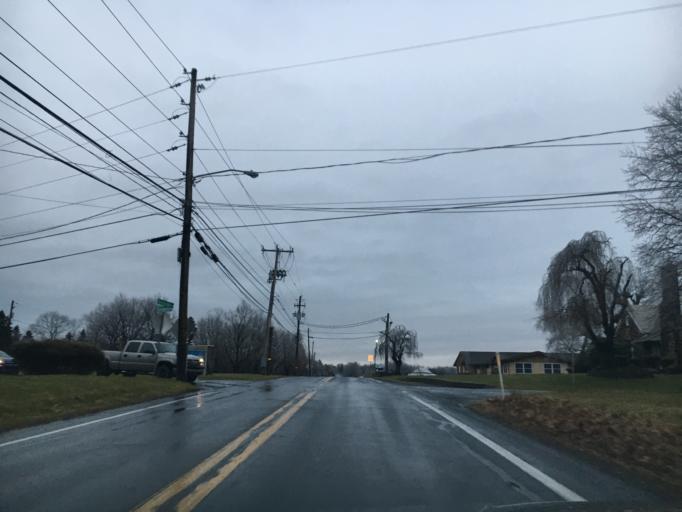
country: US
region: Pennsylvania
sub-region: Lehigh County
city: Schnecksville
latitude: 40.6329
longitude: -75.5988
